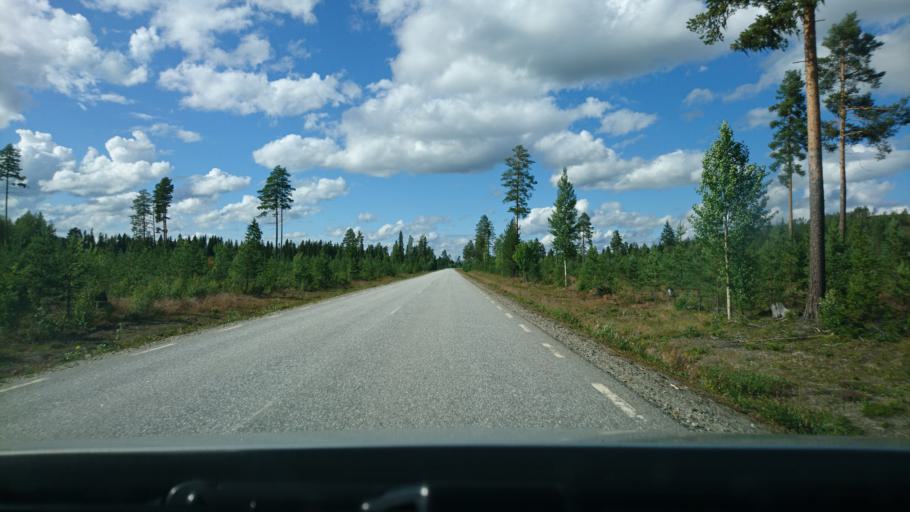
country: SE
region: Vaesterbotten
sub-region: Asele Kommun
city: Asele
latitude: 64.0461
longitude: 17.2891
